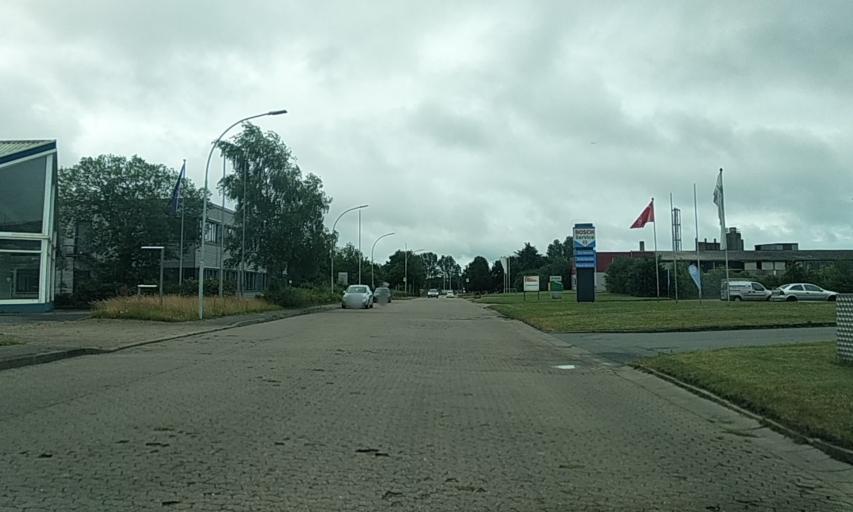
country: DE
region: Schleswig-Holstein
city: Schleswig
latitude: 54.5344
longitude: 9.5842
